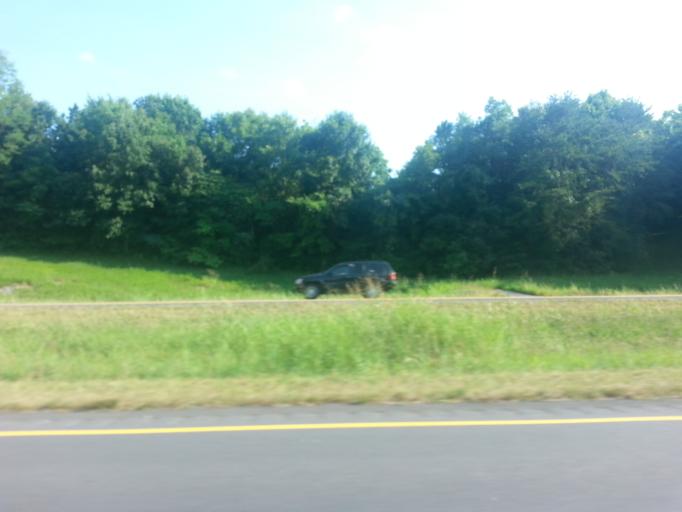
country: US
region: Tennessee
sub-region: Loudon County
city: Greenback
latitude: 35.7555
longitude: -84.1336
